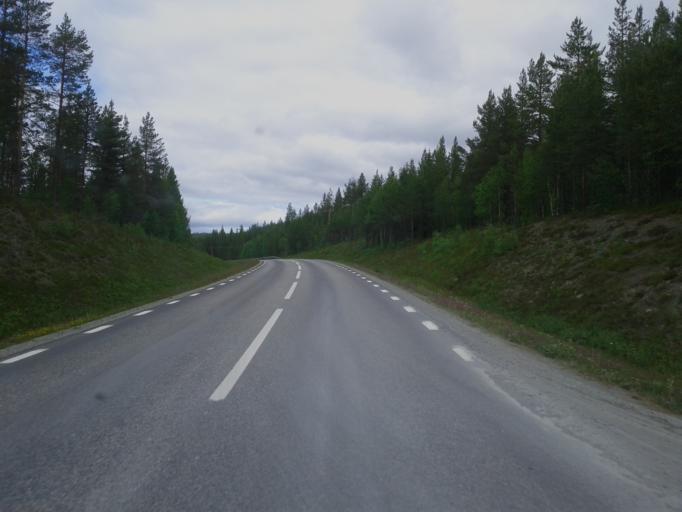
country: SE
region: Vaesterbotten
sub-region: Storumans Kommun
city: Fristad
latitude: 65.3790
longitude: 16.5137
